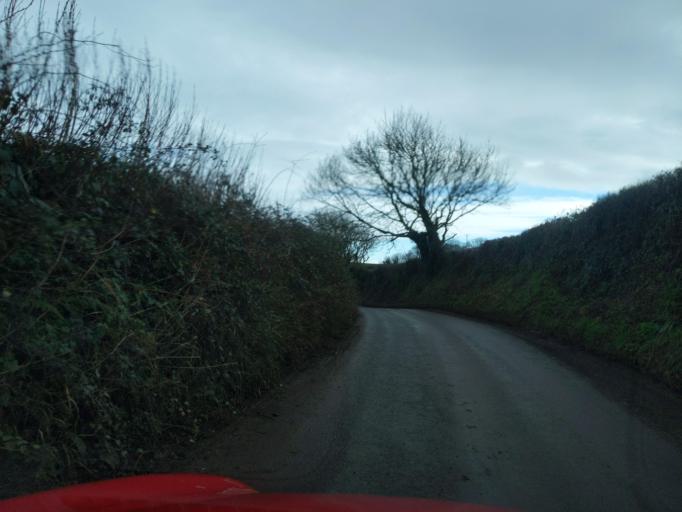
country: GB
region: England
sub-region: Devon
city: Salcombe
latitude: 50.2574
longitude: -3.6737
